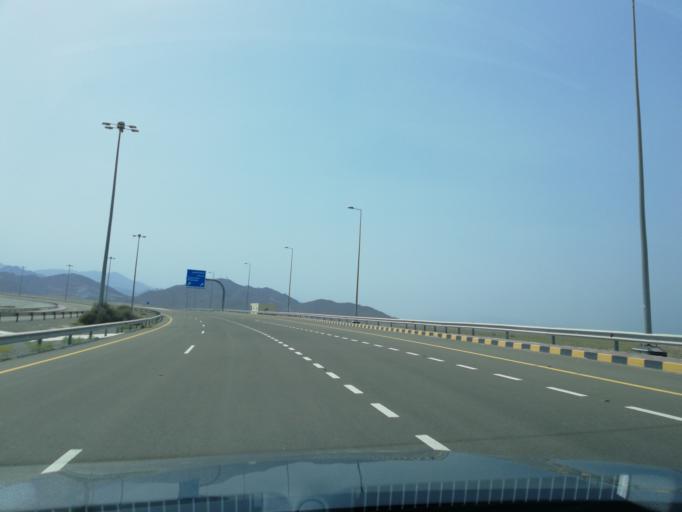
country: AE
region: Al Fujayrah
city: Al Fujayrah
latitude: 24.9521
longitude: 56.3787
